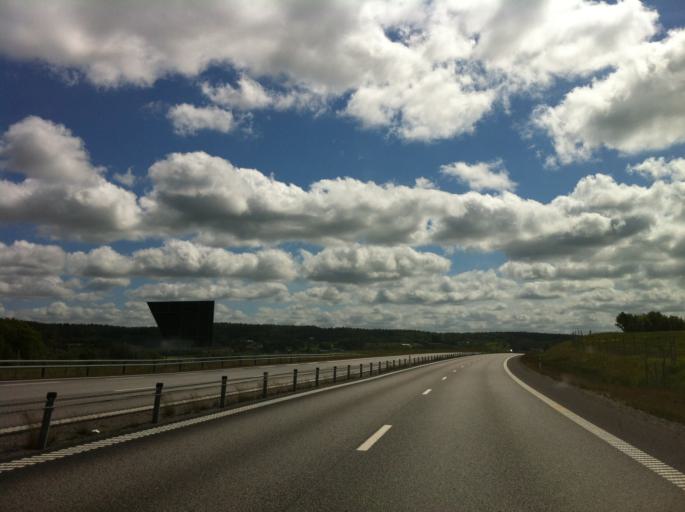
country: SE
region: Vaestra Goetaland
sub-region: Ale Kommun
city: Skepplanda
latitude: 57.9847
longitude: 12.1624
